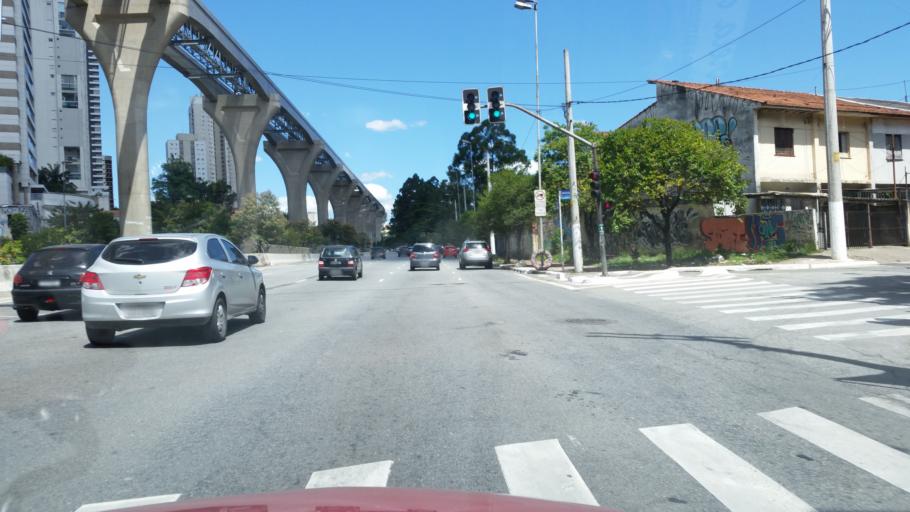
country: BR
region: Sao Paulo
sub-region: Diadema
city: Diadema
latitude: -23.6244
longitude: -46.6773
